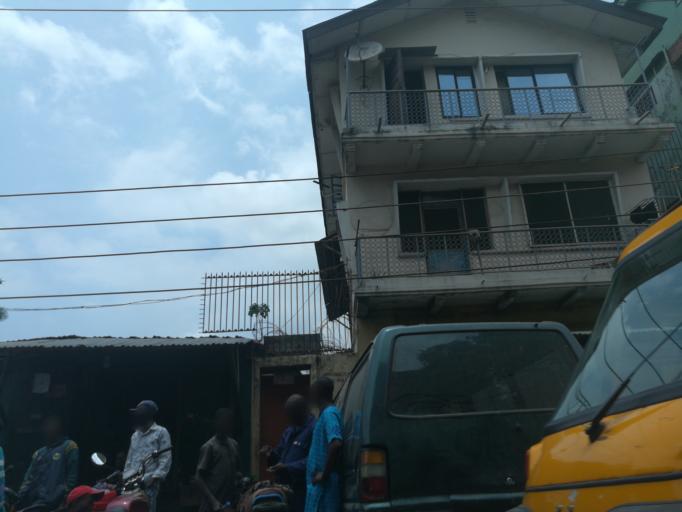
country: NG
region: Lagos
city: Lagos
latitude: 6.4546
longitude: 3.3992
